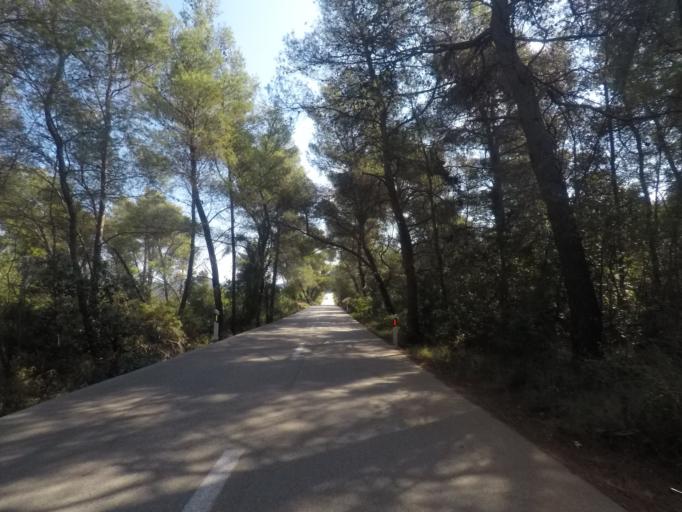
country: HR
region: Splitsko-Dalmatinska
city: Jelsa
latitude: 43.1445
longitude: 16.8067
